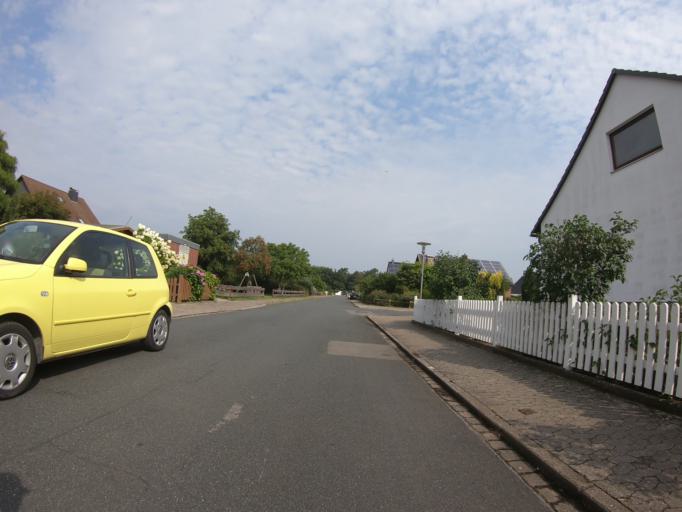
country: DE
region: Lower Saxony
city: Isenbuttel
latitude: 52.4448
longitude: 10.5662
